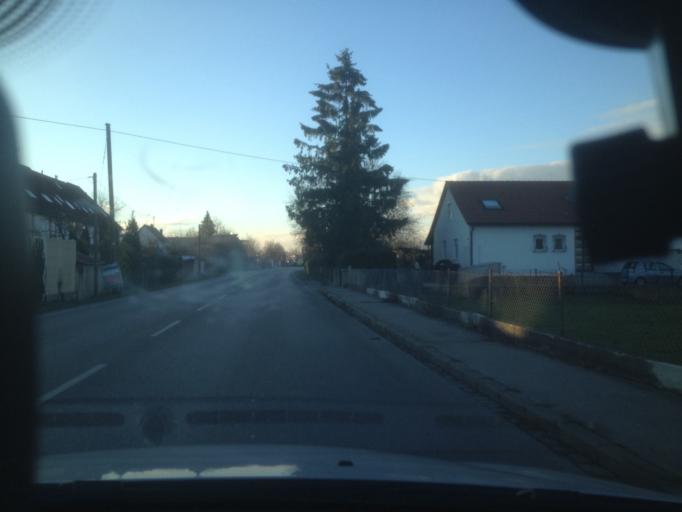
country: DE
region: Bavaria
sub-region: Swabia
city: Mering
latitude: 48.2737
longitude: 10.9829
